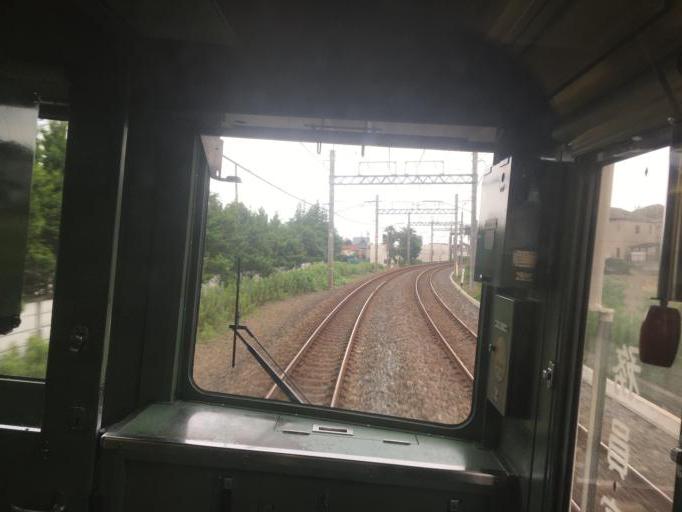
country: JP
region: Saitama
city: Iwatsuki
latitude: 35.9579
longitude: 139.7059
